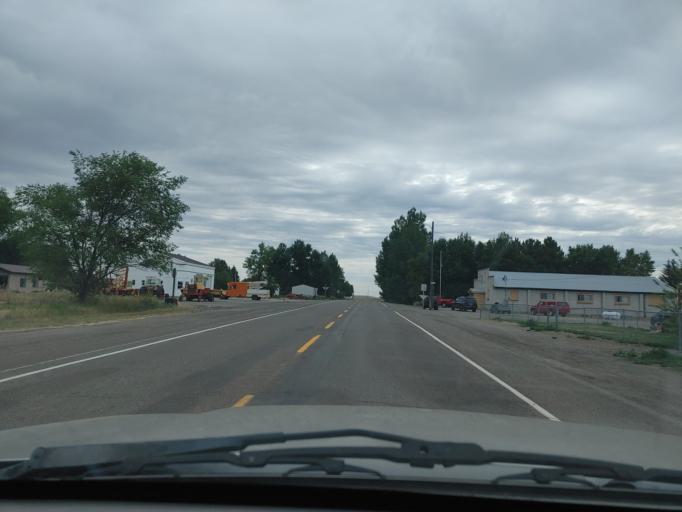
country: US
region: Idaho
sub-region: Lincoln County
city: Shoshone
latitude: 43.0493
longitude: -114.1531
